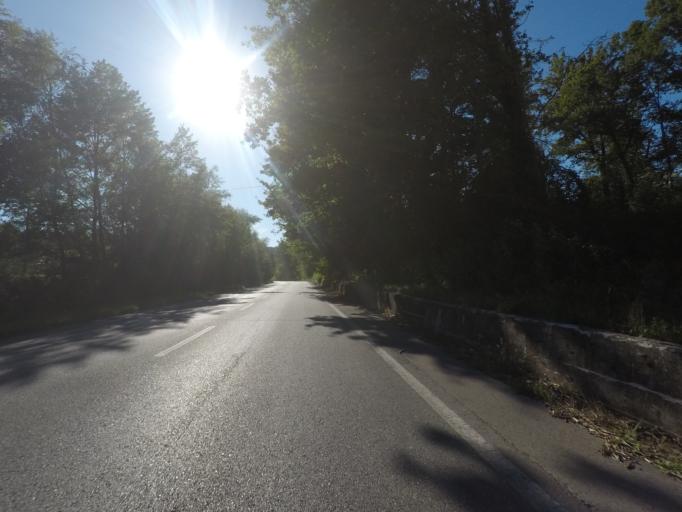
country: IT
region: Tuscany
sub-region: Provincia di Lucca
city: San Martino in Freddana-Monsagrati
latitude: 43.9003
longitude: 10.4040
